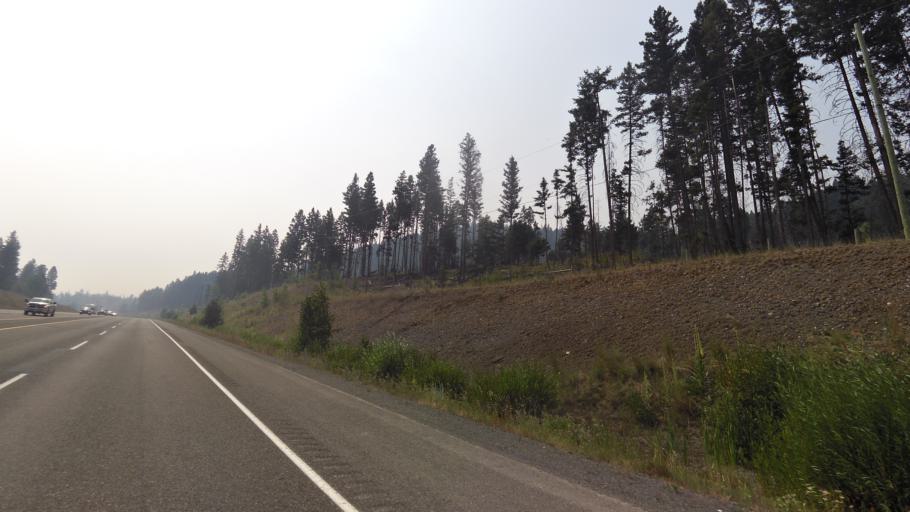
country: CA
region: British Columbia
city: Merritt
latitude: 50.0192
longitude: -120.6239
